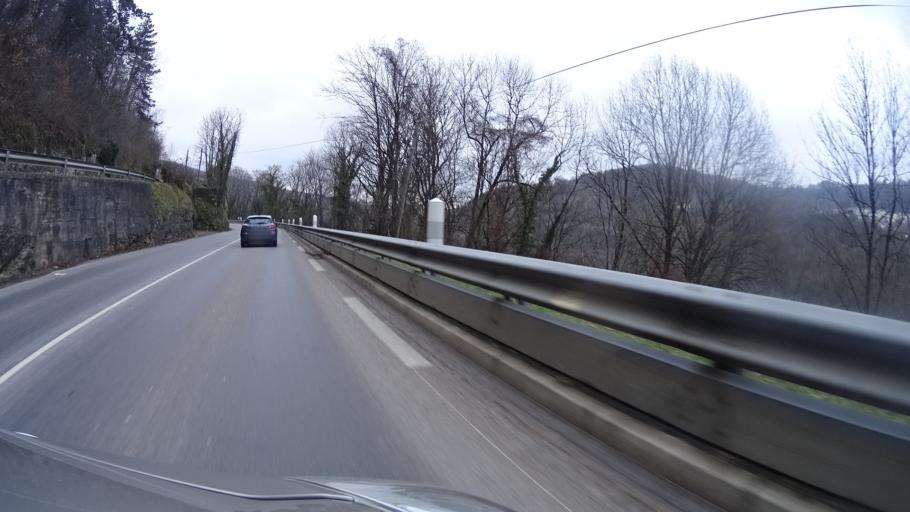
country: FR
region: Franche-Comte
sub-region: Departement du Doubs
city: Morre
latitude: 47.2287
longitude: 6.0623
